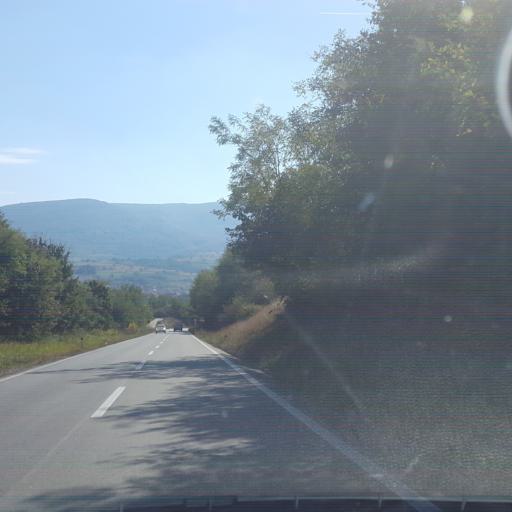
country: RS
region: Central Serbia
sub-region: Nisavski Okrug
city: Svrljig
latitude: 43.4203
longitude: 22.1306
